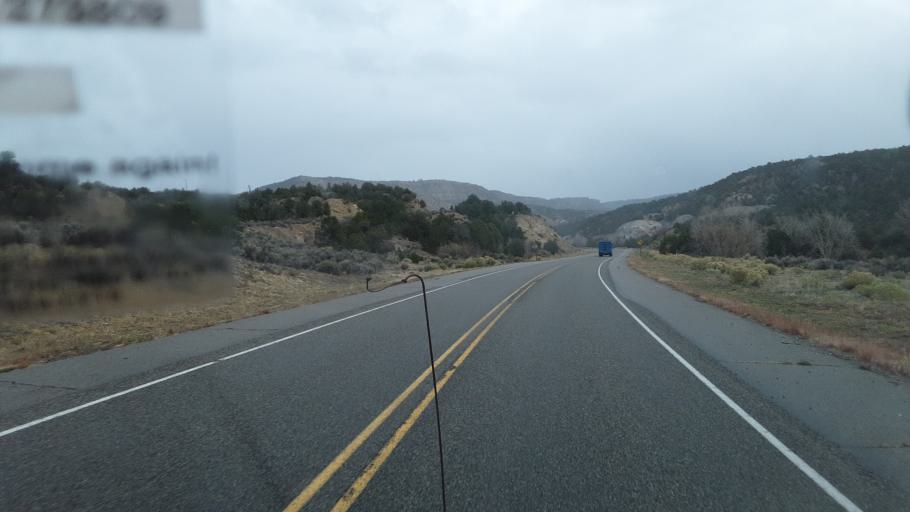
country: US
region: New Mexico
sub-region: Rio Arriba County
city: Santa Teresa
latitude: 36.3867
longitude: -106.4990
